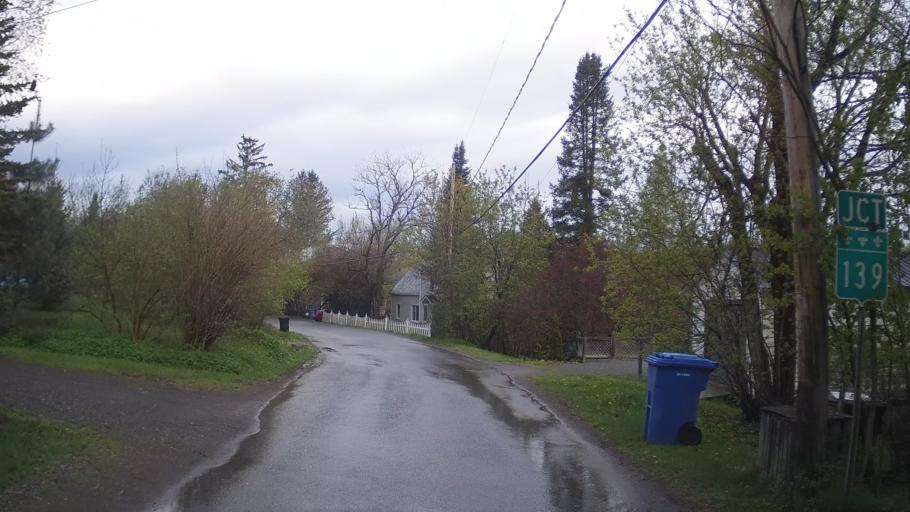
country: CA
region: Quebec
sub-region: Monteregie
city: Sutton
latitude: 45.1757
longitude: -72.6587
